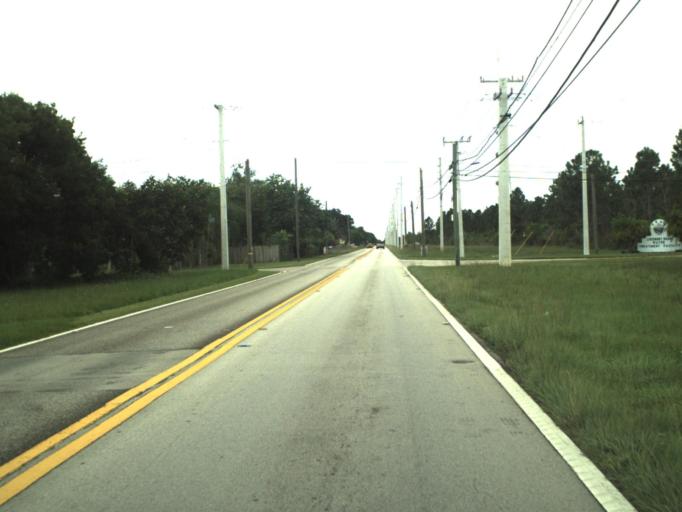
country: US
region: Florida
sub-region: Miami-Dade County
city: Florida City
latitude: 25.4392
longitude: -80.5016
